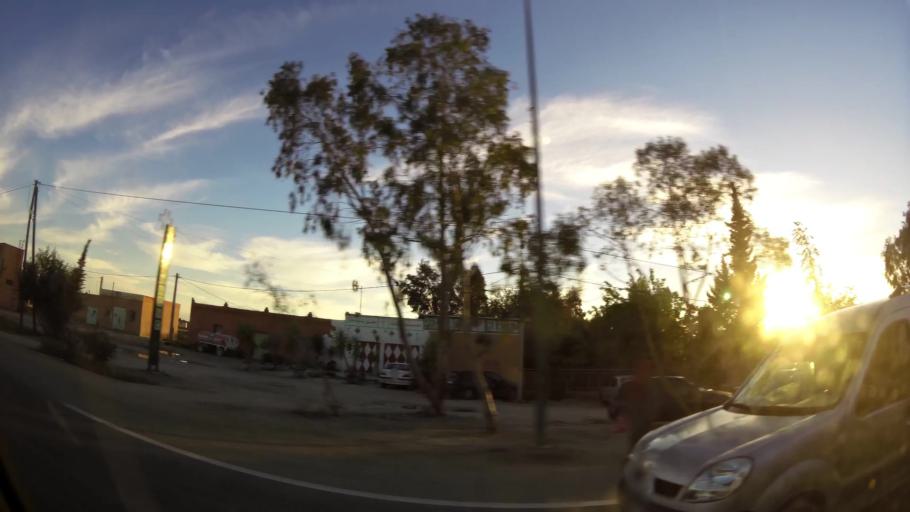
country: MA
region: Marrakech-Tensift-Al Haouz
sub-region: Marrakech
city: Marrakesh
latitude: 31.7608
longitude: -8.1154
